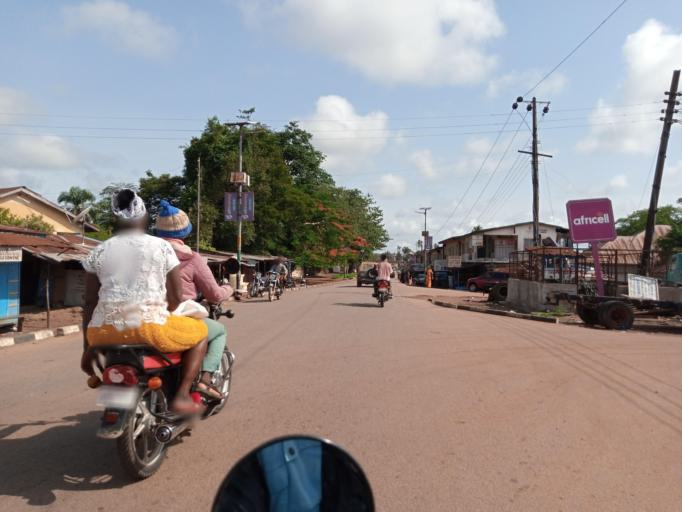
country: SL
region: Southern Province
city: Bo
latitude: 7.9619
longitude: -11.7341
